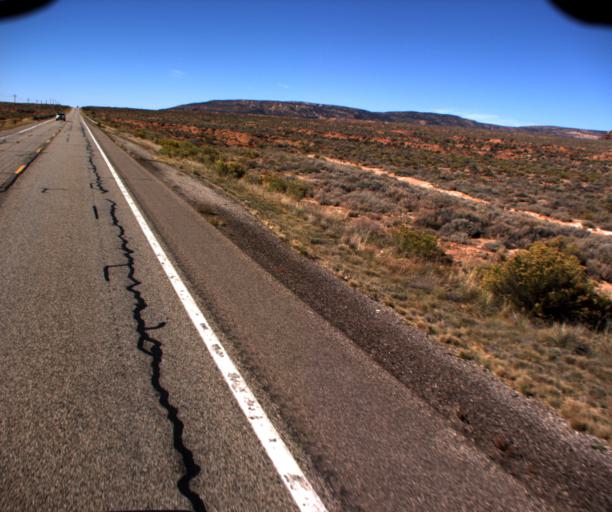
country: US
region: Arizona
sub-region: Coconino County
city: Fredonia
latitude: 36.8757
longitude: -112.6615
